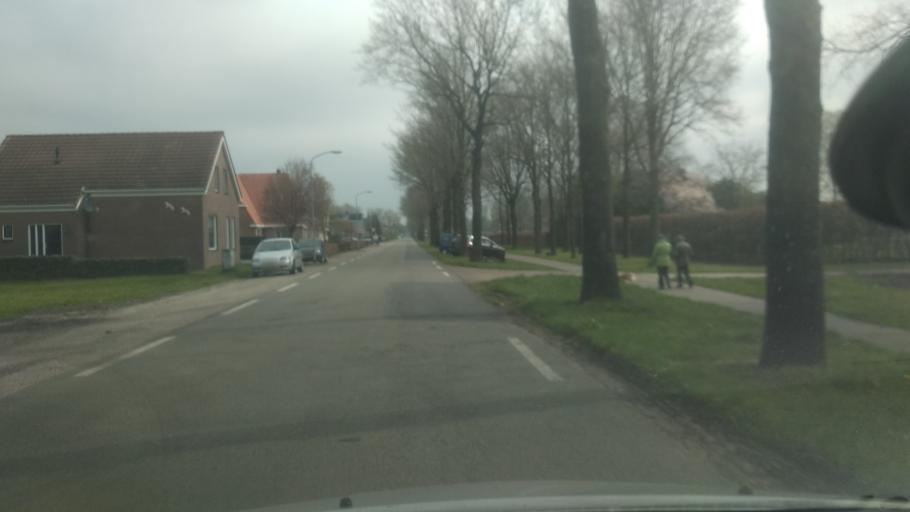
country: NL
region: Groningen
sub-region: Gemeente Stadskanaal
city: Stadskanaal
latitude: 52.9242
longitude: 6.9740
